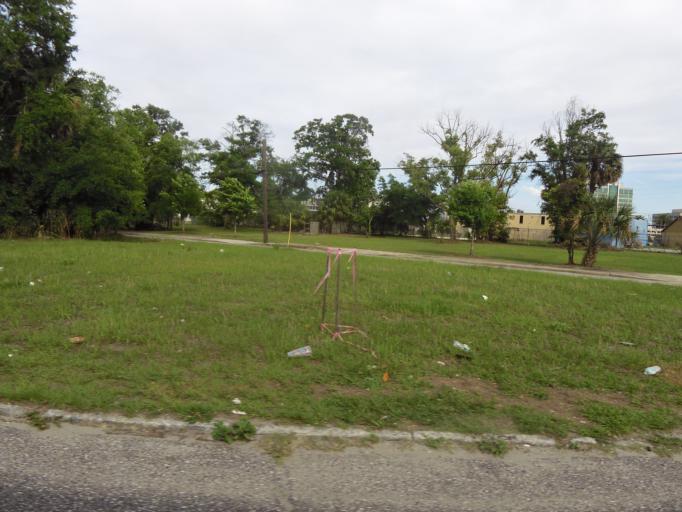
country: US
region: Florida
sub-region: Duval County
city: Jacksonville
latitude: 30.3236
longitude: -81.6784
